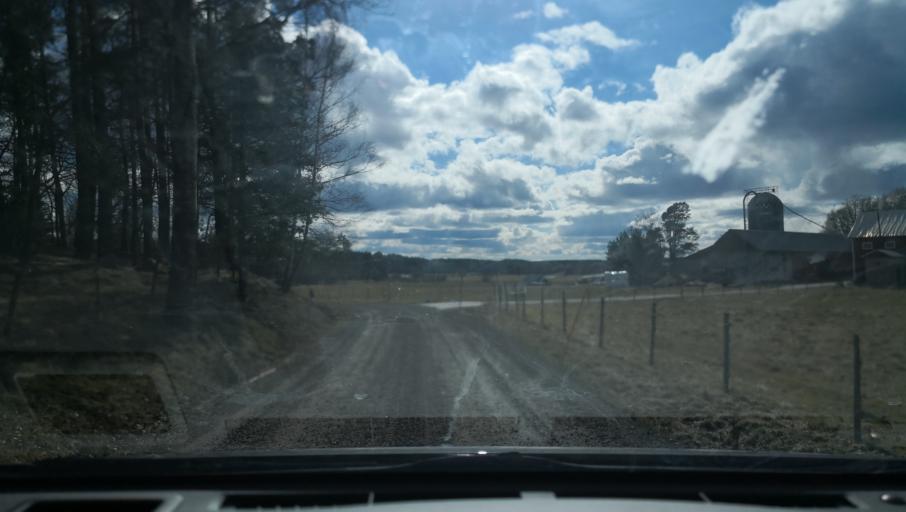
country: SE
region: OErebro
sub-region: Lindesbergs Kommun
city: Fellingsbro
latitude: 59.4144
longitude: 15.6768
